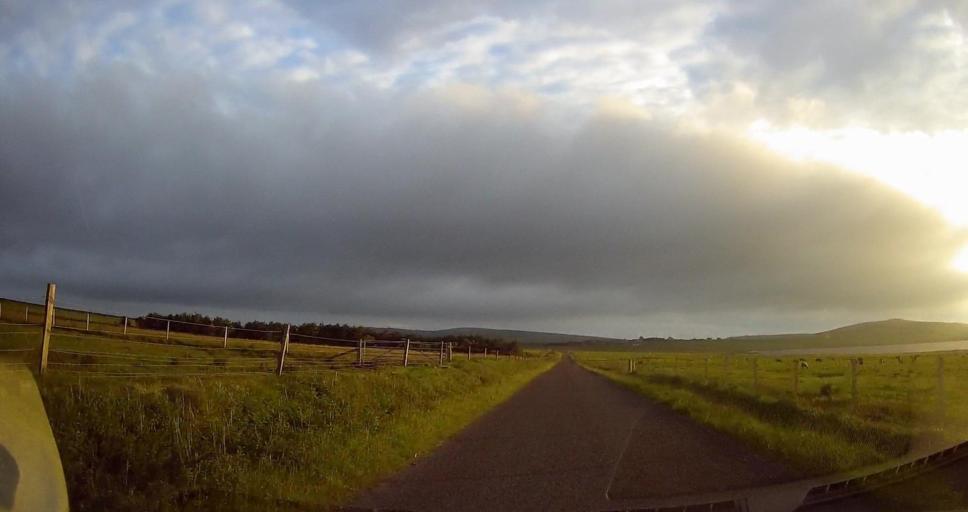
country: GB
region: Scotland
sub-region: Orkney Islands
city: Stromness
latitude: 59.1054
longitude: -3.2495
